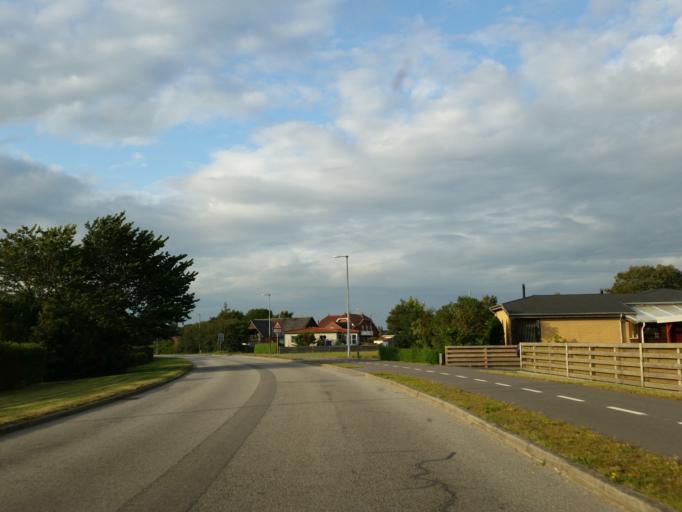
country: DK
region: South Denmark
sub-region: Tonder Kommune
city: Sherrebek
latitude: 55.1543
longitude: 8.7602
